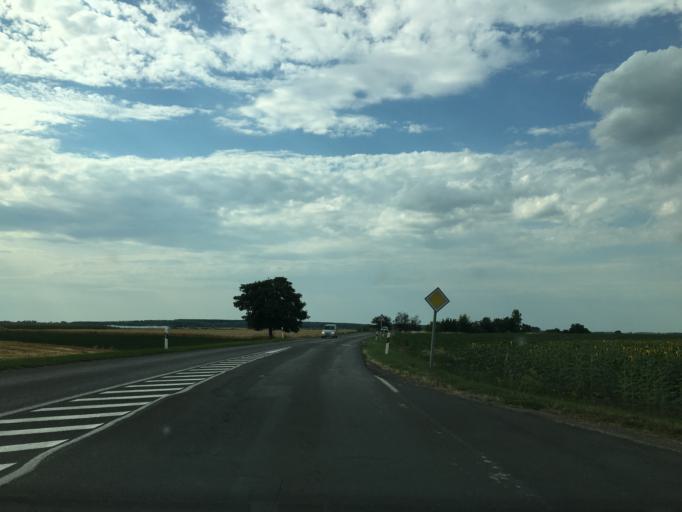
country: HU
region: Bacs-Kiskun
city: Dusnok
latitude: 46.4204
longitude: 18.9424
